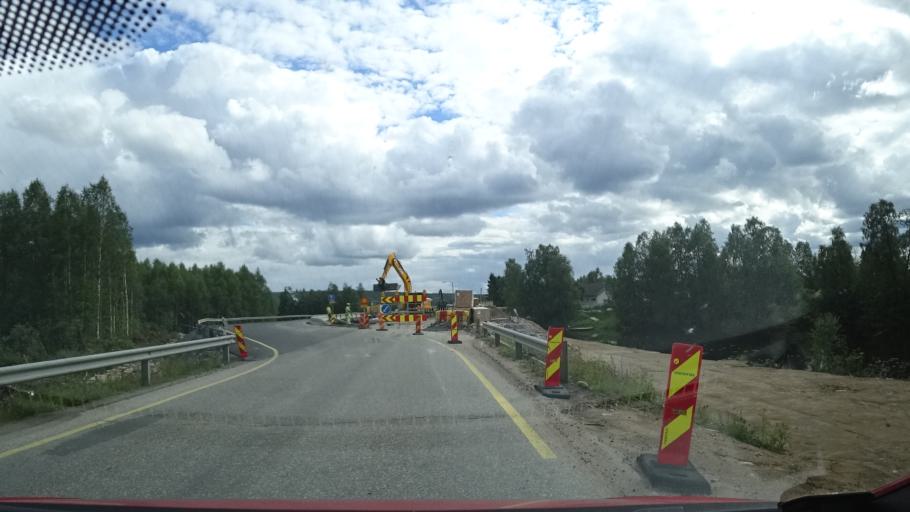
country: FI
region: Lapland
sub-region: Rovaniemi
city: Rovaniemi
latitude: 66.5245
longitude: 25.7443
